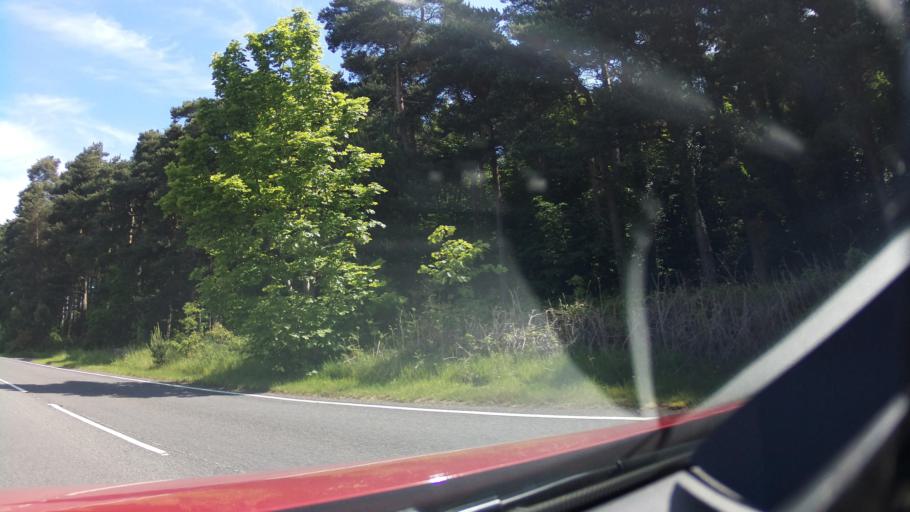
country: GB
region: England
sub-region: North Lincolnshire
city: Manton
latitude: 53.5268
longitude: -0.5785
